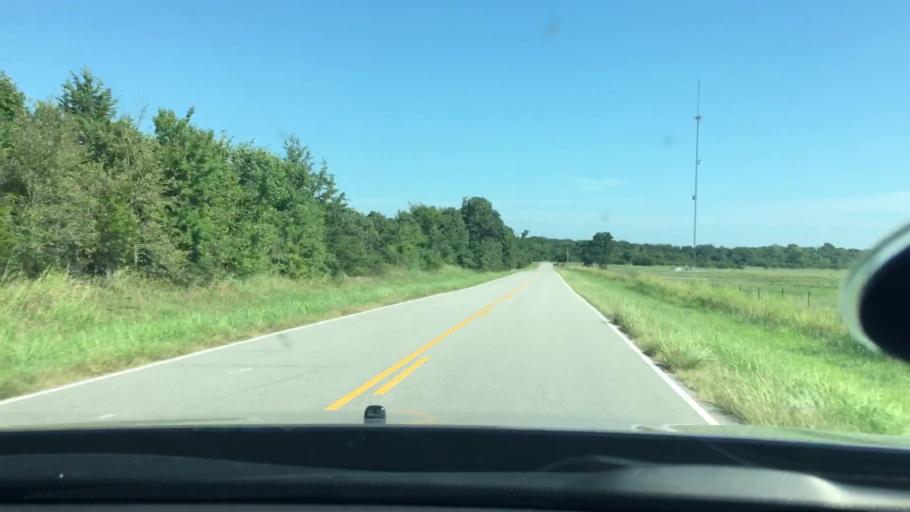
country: US
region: Oklahoma
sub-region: Johnston County
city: Tishomingo
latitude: 34.3561
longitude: -96.5488
